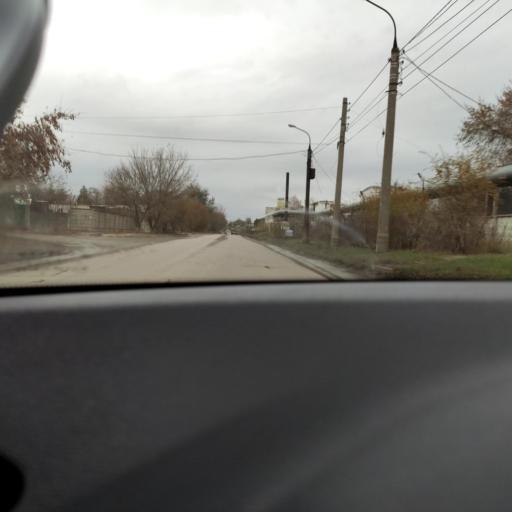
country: RU
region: Samara
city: Smyshlyayevka
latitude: 53.2024
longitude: 50.2942
